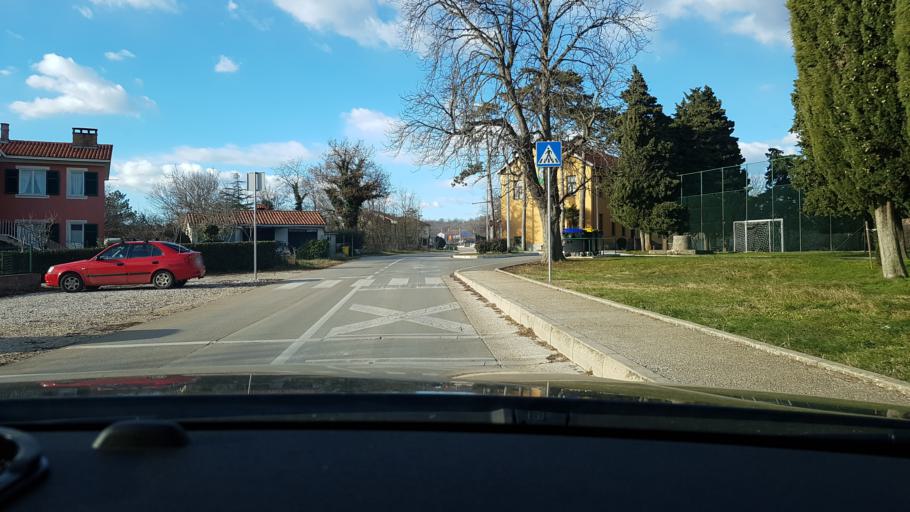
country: HR
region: Istarska
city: Vinez
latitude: 45.1011
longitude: 14.1051
